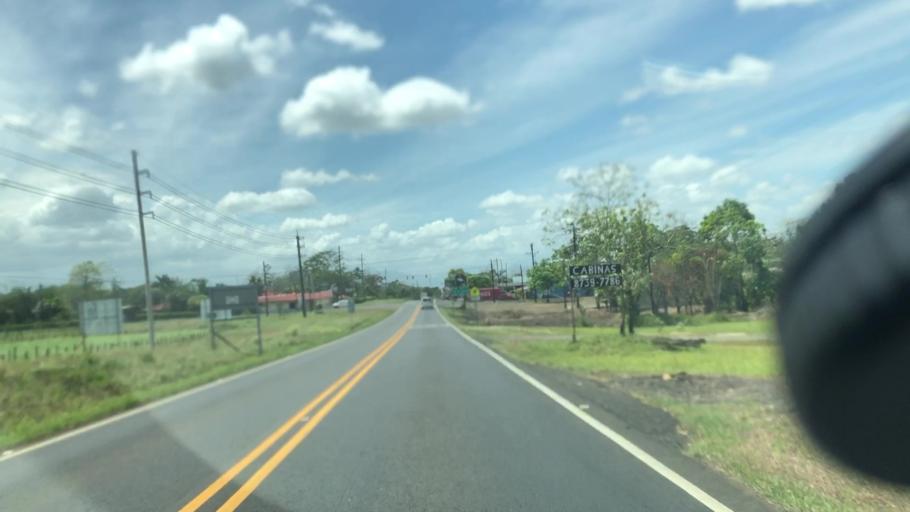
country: CR
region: Alajuela
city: Pital
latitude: 10.4568
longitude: -84.4056
